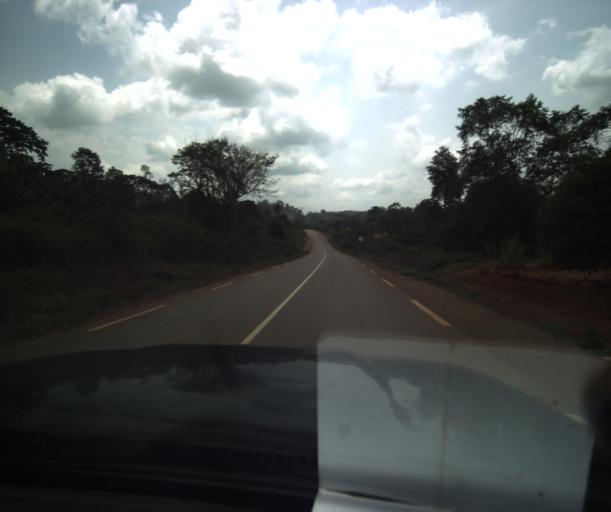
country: CM
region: Centre
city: Mbankomo
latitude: 3.7875
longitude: 11.4183
